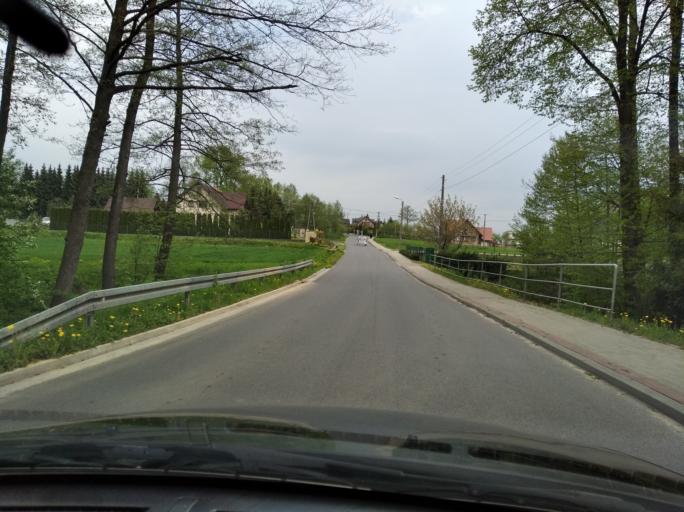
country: PL
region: Lesser Poland Voivodeship
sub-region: Powiat tarnowski
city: Skrzyszow
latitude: 49.9503
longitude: 21.0330
